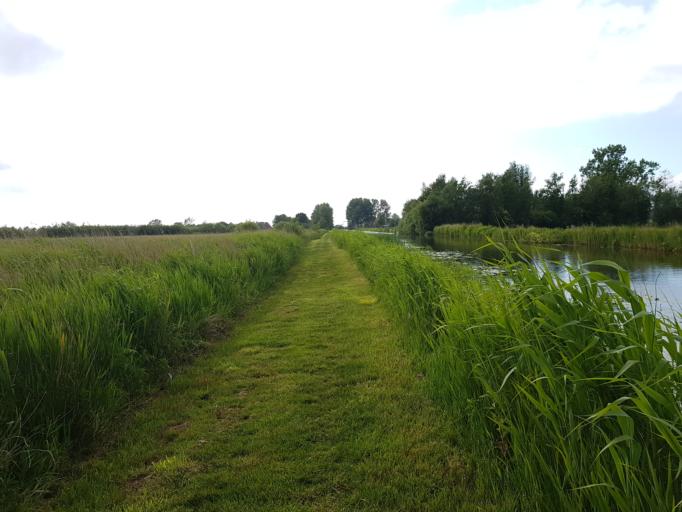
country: NL
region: Friesland
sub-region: Gemeente Smallingerland
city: Oudega
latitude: 53.0943
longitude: 5.9576
